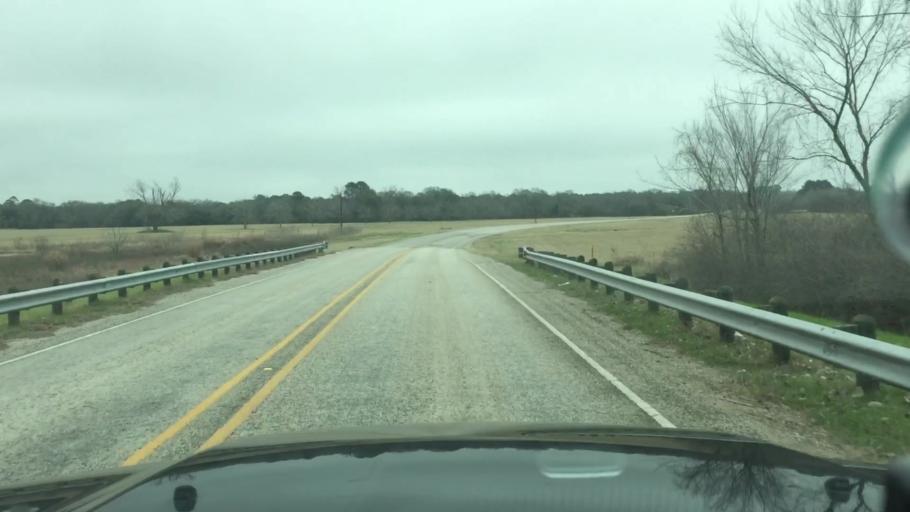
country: US
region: Texas
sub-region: Fayette County
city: La Grange
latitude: 30.0113
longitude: -96.9157
